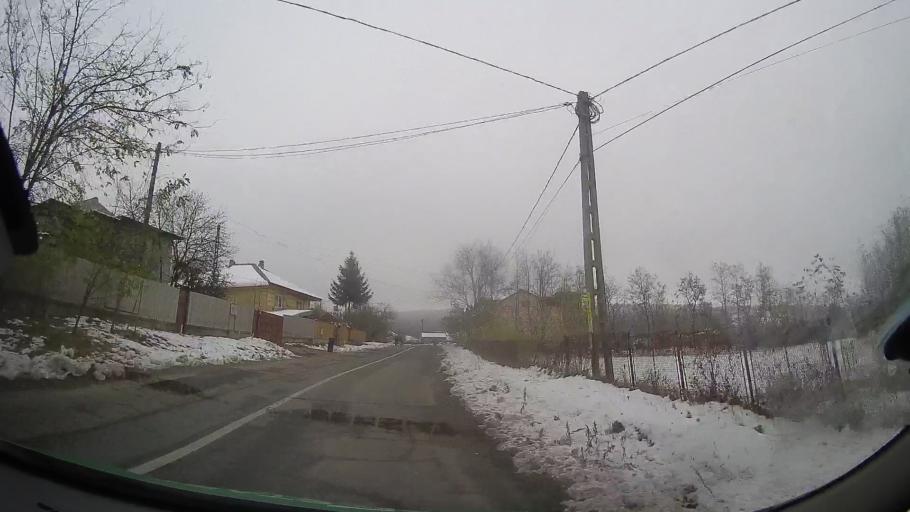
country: RO
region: Bacau
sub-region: Comuna Podu Turcului
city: Podu Turcului
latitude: 46.2036
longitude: 27.3887
